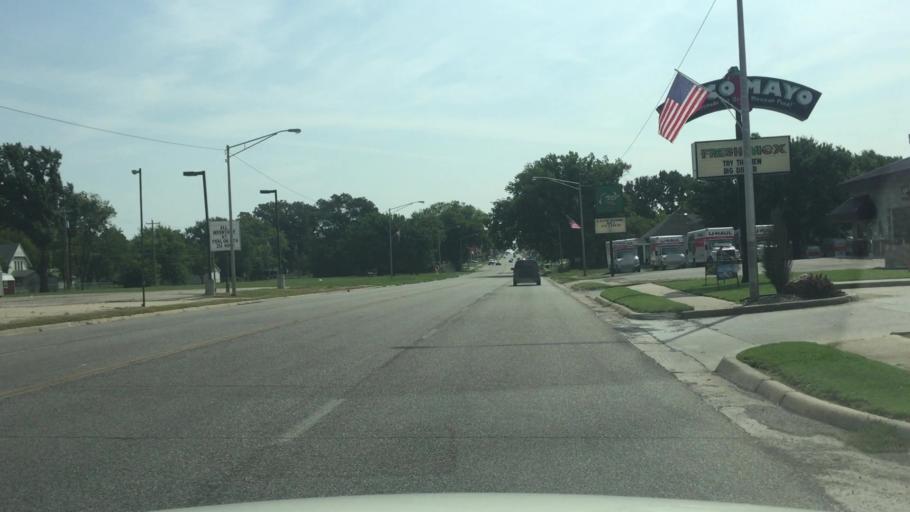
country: US
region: Kansas
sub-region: Montgomery County
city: Coffeyville
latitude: 37.0330
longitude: -95.6343
